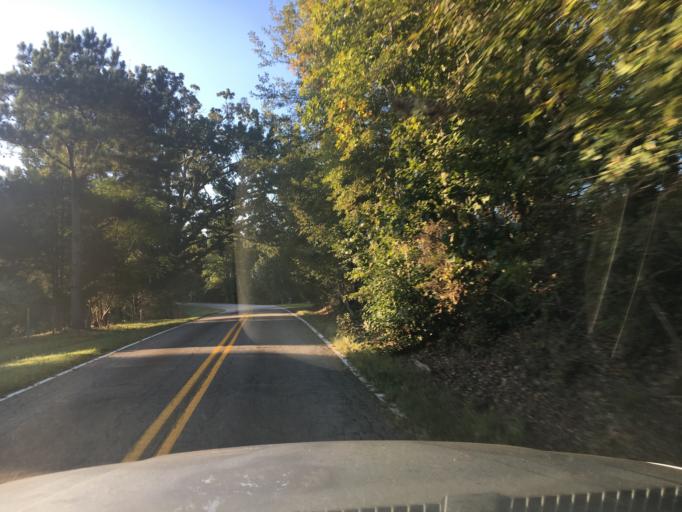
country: US
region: South Carolina
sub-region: Spartanburg County
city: Woodruff
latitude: 34.7812
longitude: -81.9856
